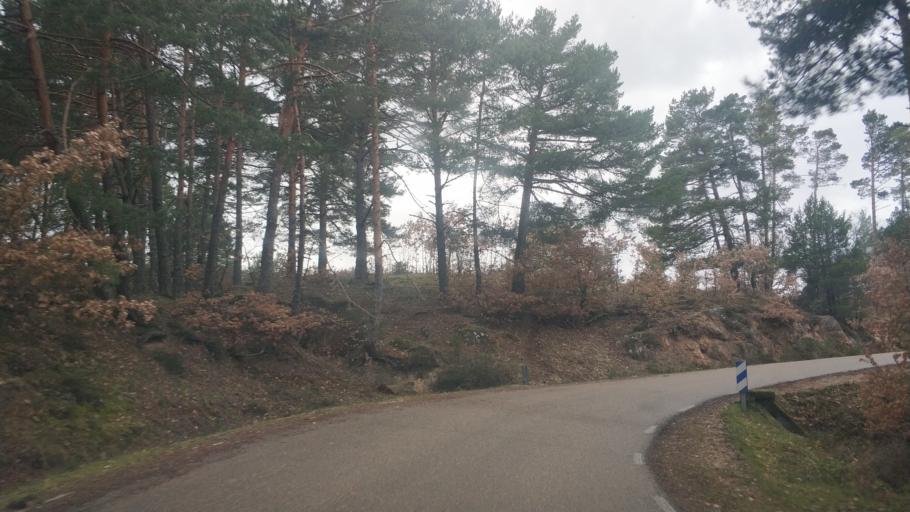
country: ES
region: Castille and Leon
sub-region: Provincia de Burgos
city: Canicosa de la Sierra
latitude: 41.9309
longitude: -3.0383
